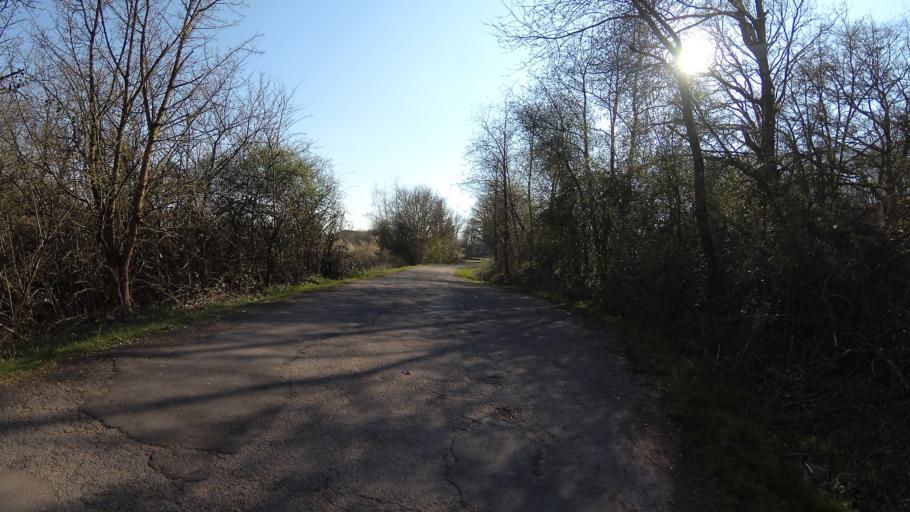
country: DE
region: Saarland
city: Ottweiler
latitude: 49.3876
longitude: 7.1657
